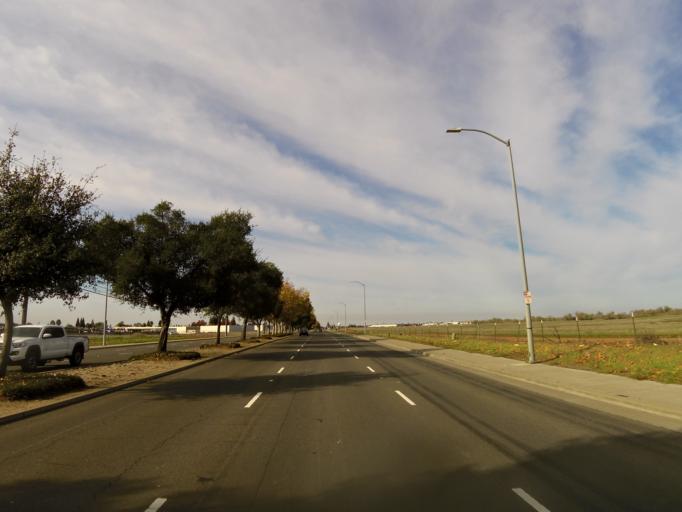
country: US
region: California
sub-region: Sacramento County
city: Rancho Cordova
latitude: 38.5651
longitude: -121.2484
